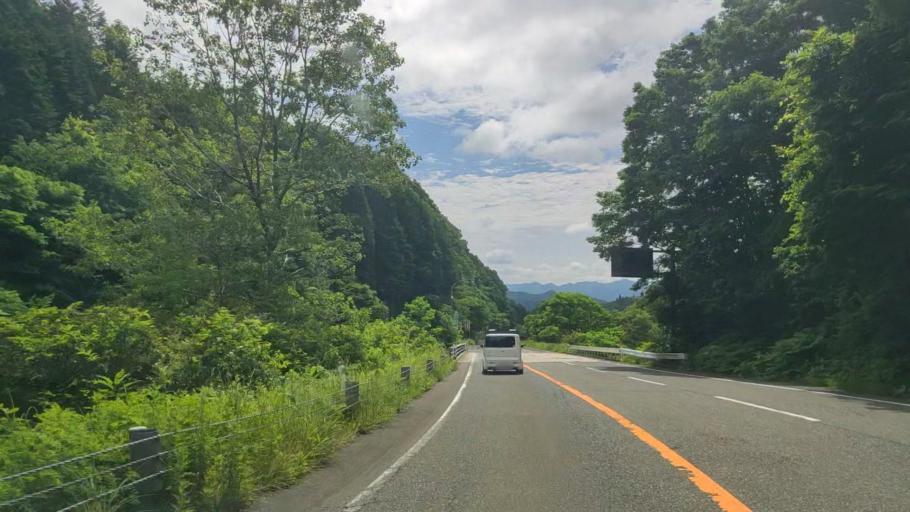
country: JP
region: Okayama
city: Niimi
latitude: 35.1832
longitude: 133.5361
